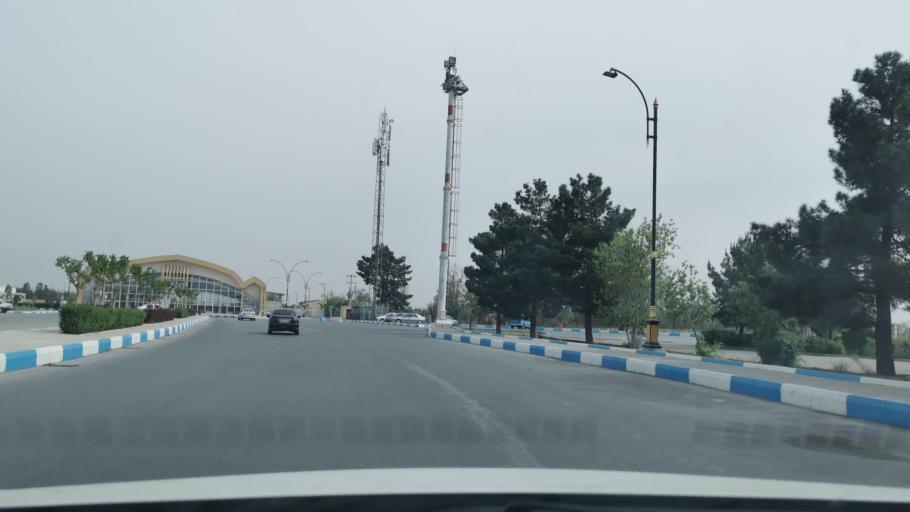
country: IR
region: Razavi Khorasan
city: Mashhad
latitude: 36.2263
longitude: 59.6394
